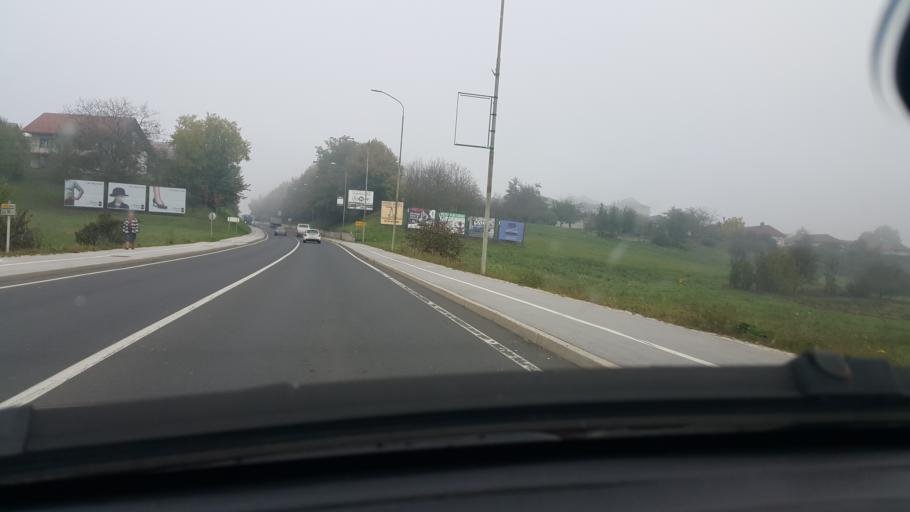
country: SI
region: Brezice
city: Brezice
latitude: 45.9014
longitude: 15.6042
